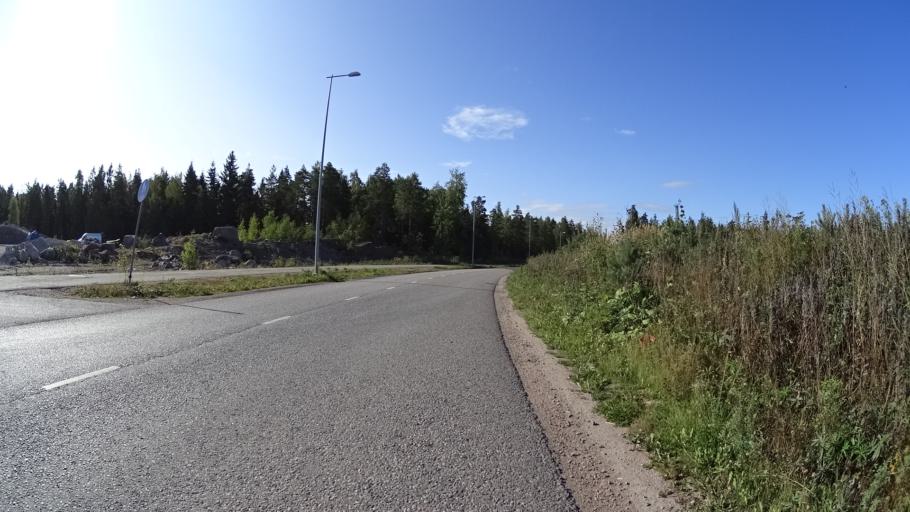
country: FI
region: Uusimaa
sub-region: Helsinki
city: Kilo
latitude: 60.2892
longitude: 24.7657
